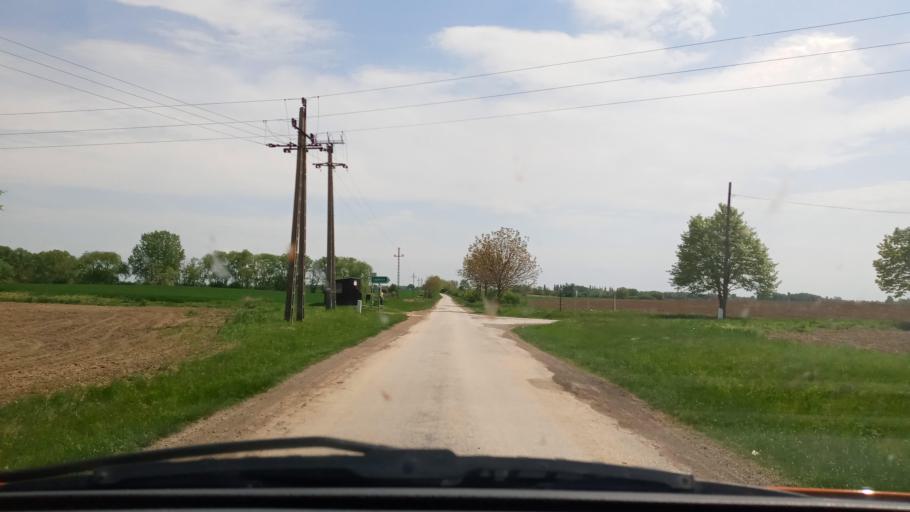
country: HU
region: Baranya
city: Villany
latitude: 45.8214
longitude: 18.5060
